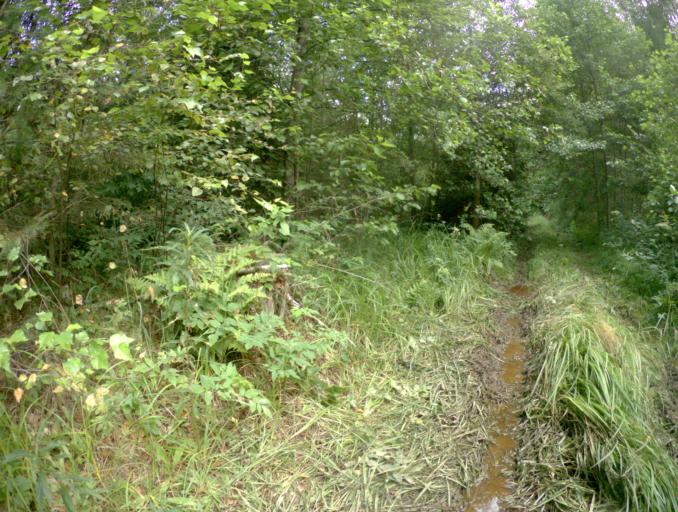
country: RU
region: Vladimir
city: Orgtrud
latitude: 56.0801
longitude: 40.5970
